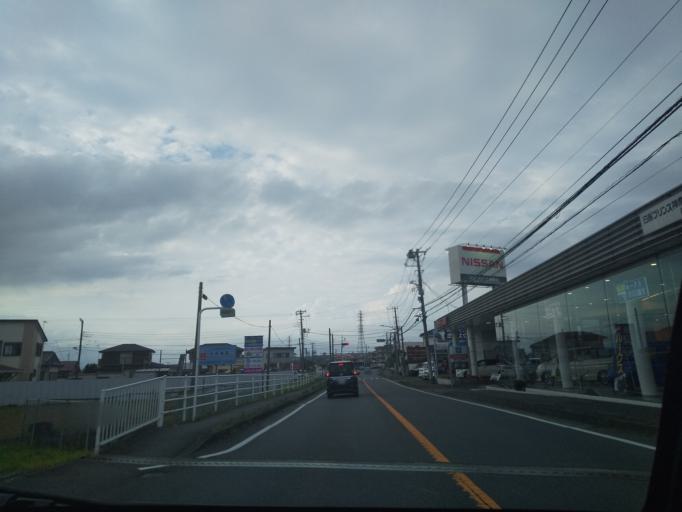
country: JP
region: Kanagawa
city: Zama
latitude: 35.4762
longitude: 139.3890
